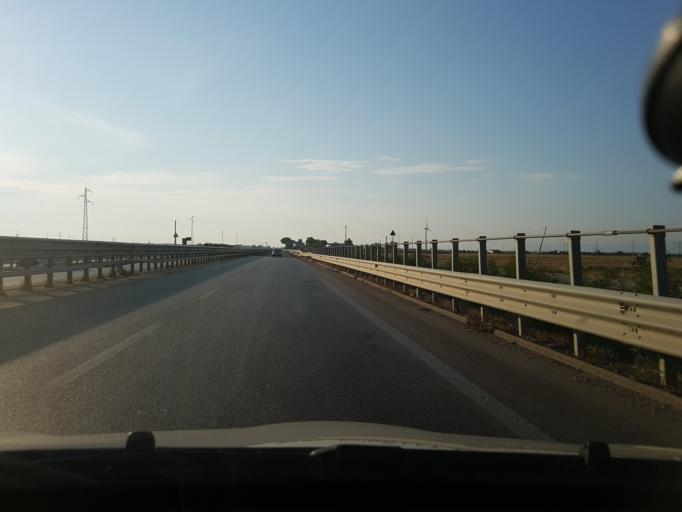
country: IT
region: Apulia
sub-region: Provincia di Foggia
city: Carapelle
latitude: 41.3757
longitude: 15.6833
